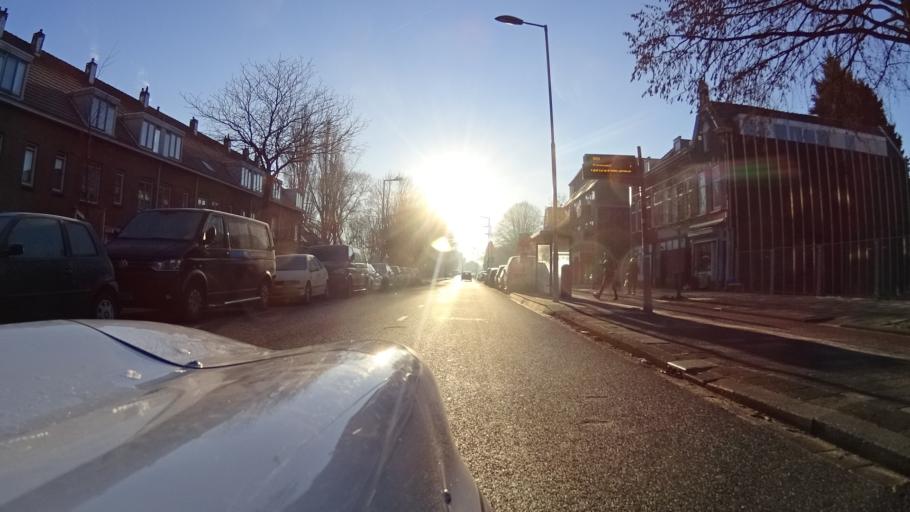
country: NL
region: South Holland
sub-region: Gemeente Rotterdam
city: Rotterdam
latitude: 51.8864
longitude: 4.4986
